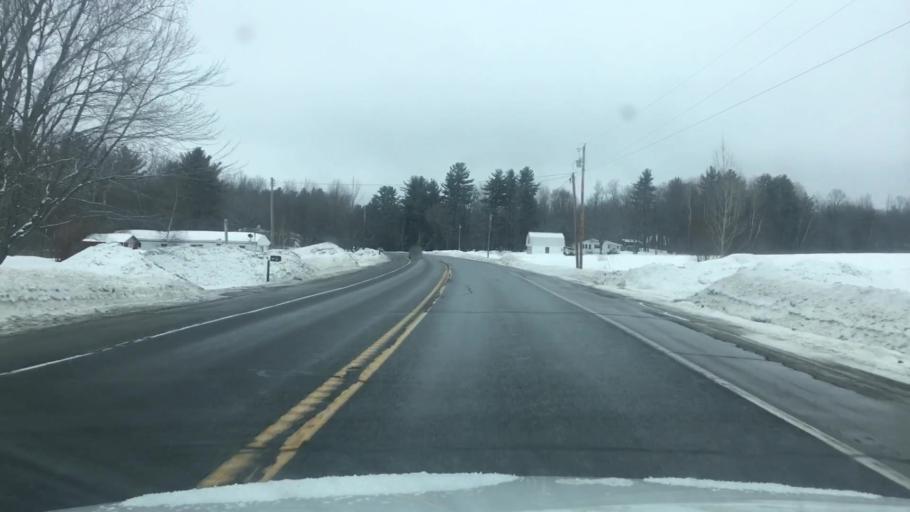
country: US
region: Maine
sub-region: Franklin County
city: New Sharon
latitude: 44.6544
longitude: -69.9589
